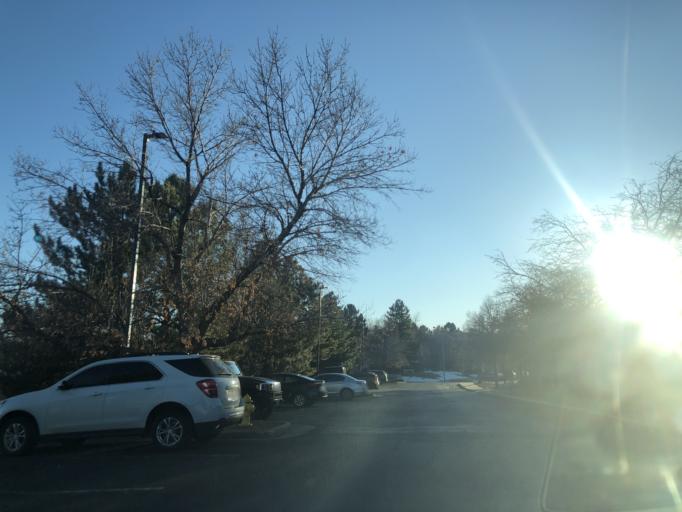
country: US
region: Colorado
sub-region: Adams County
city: Aurora
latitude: 39.7200
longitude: -104.8140
